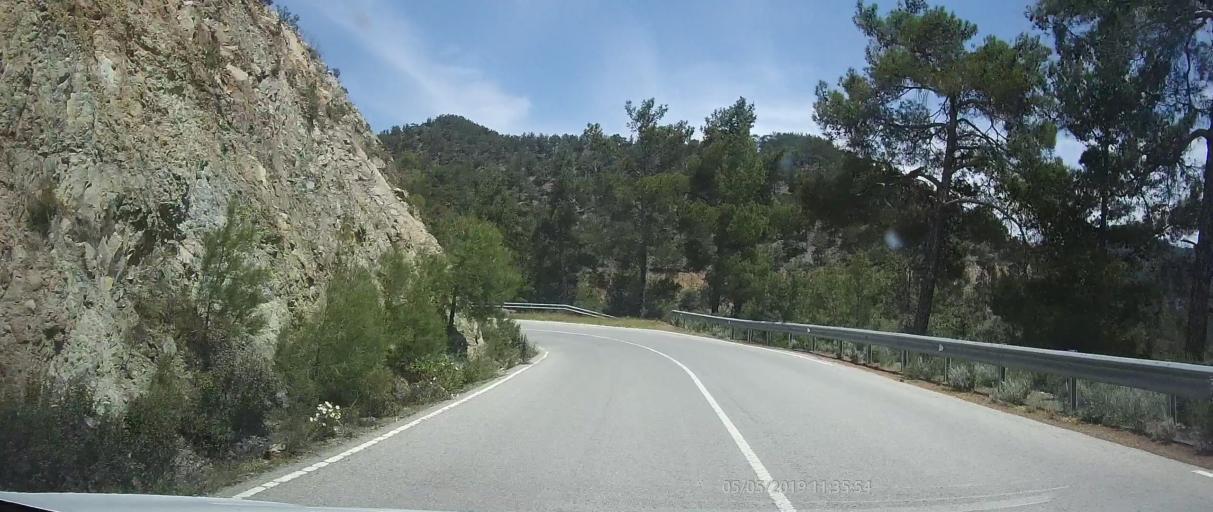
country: CY
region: Lefkosia
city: Kato Pyrgos
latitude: 34.9706
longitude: 32.6517
